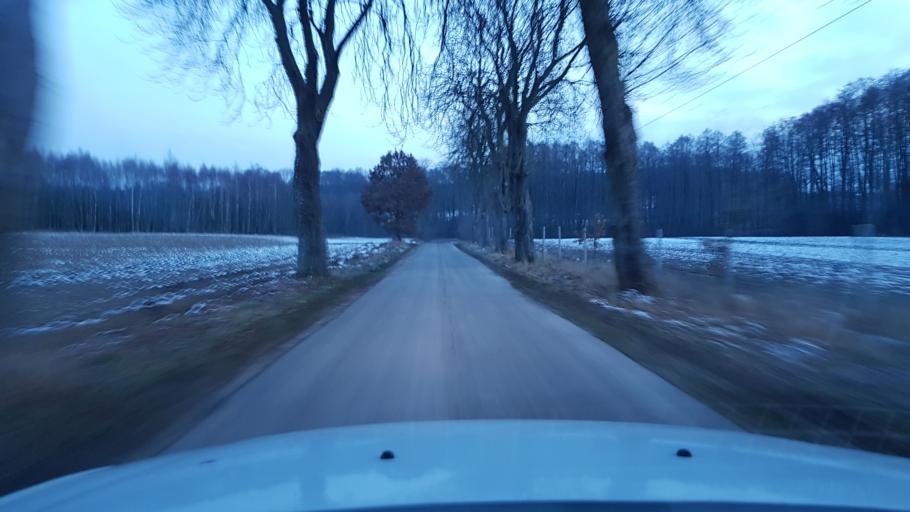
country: PL
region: West Pomeranian Voivodeship
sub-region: Powiat swidwinski
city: Slawoborze
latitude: 53.9349
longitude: 15.7251
